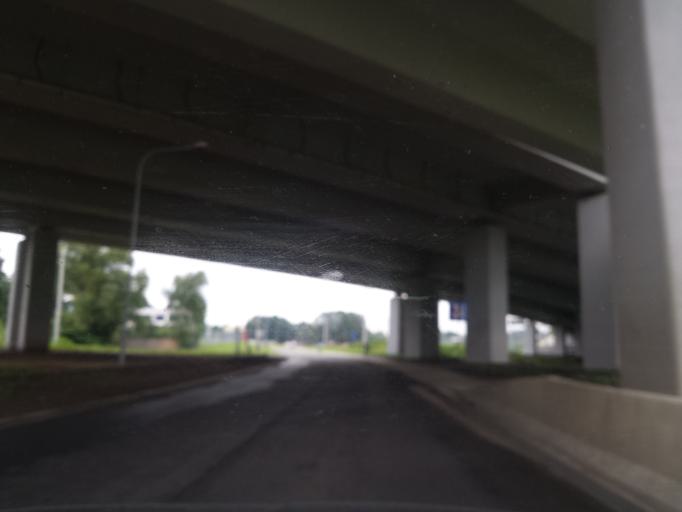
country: PL
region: Silesian Voivodeship
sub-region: Powiat bielski
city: Bystra
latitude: 49.7866
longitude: 19.0681
